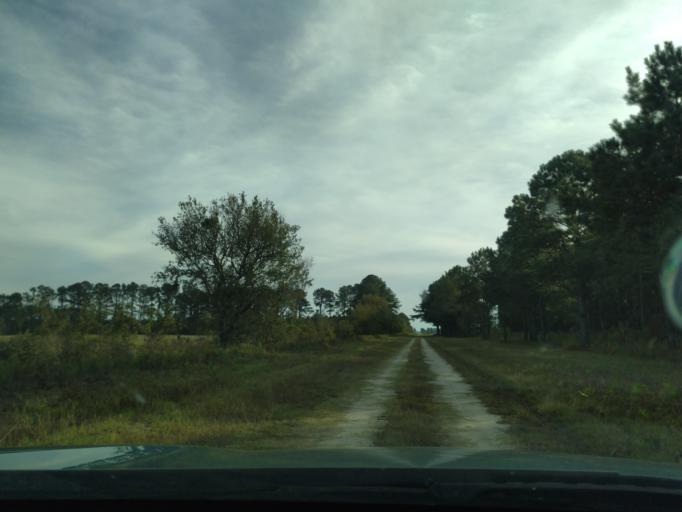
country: US
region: North Carolina
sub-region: Beaufort County
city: Belhaven
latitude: 35.6637
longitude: -76.5493
